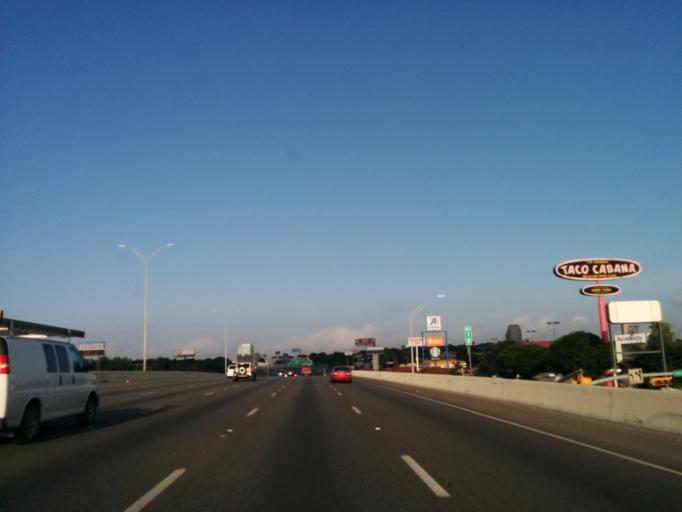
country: US
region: Texas
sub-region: Bexar County
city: Castle Hills
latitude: 29.5119
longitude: -98.5349
